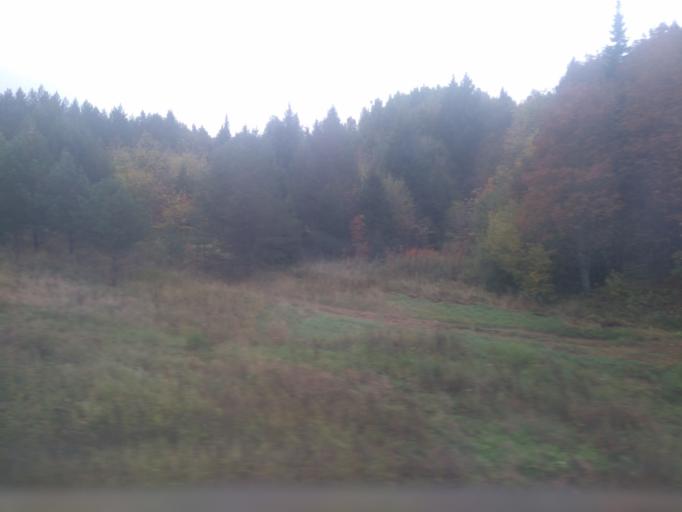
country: RU
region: Udmurtiya
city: Alnashi
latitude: 56.2342
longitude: 52.7205
